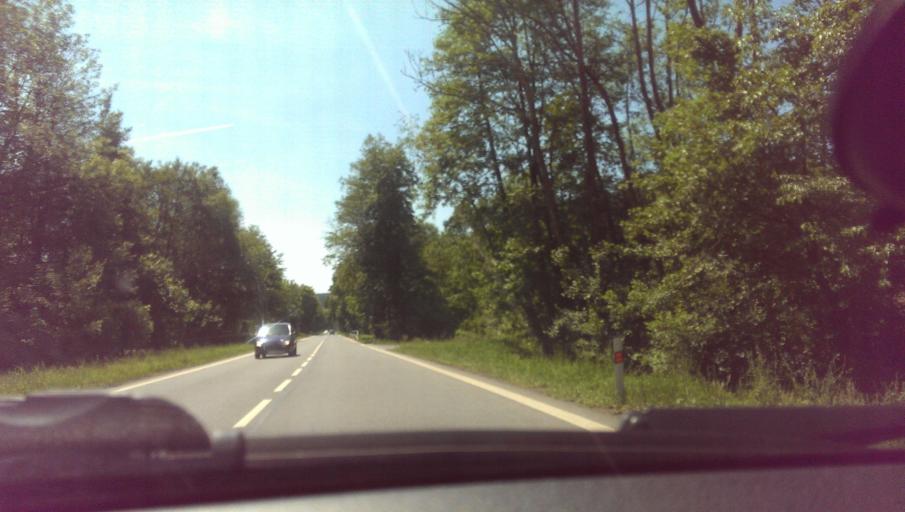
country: CZ
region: Zlin
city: Breznice
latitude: 49.1766
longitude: 17.6400
